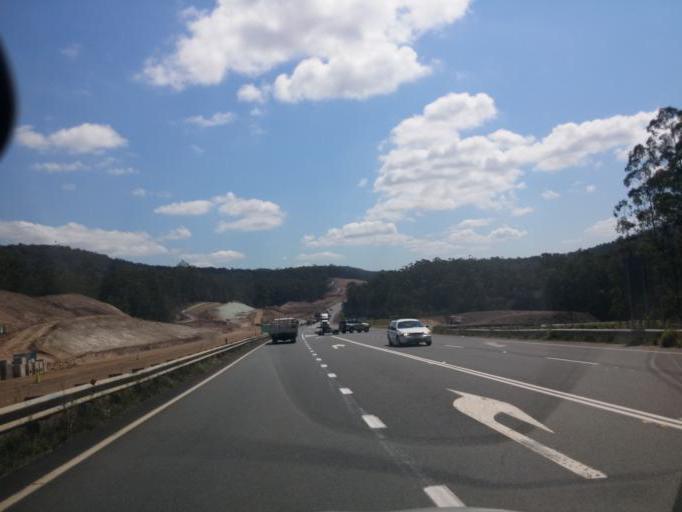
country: AU
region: New South Wales
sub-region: Port Macquarie-Hastings
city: North Shore
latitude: -31.2774
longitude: 152.8128
